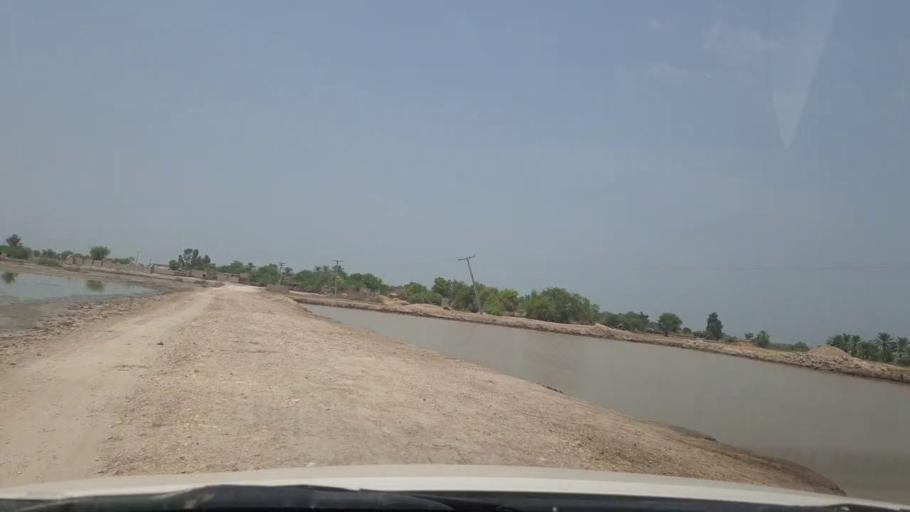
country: PK
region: Sindh
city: Rustam jo Goth
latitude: 28.0402
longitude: 68.7539
